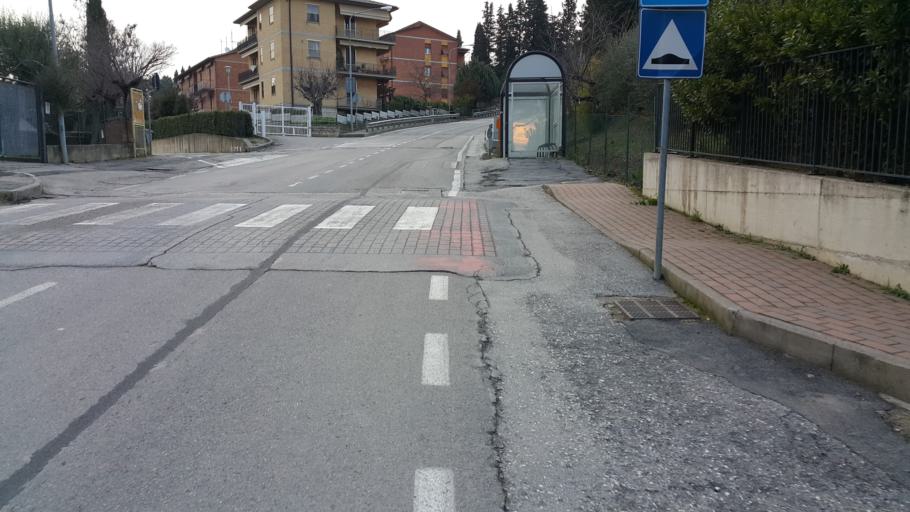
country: IT
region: Umbria
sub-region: Provincia di Perugia
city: Perugia
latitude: 43.0876
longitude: 12.3718
